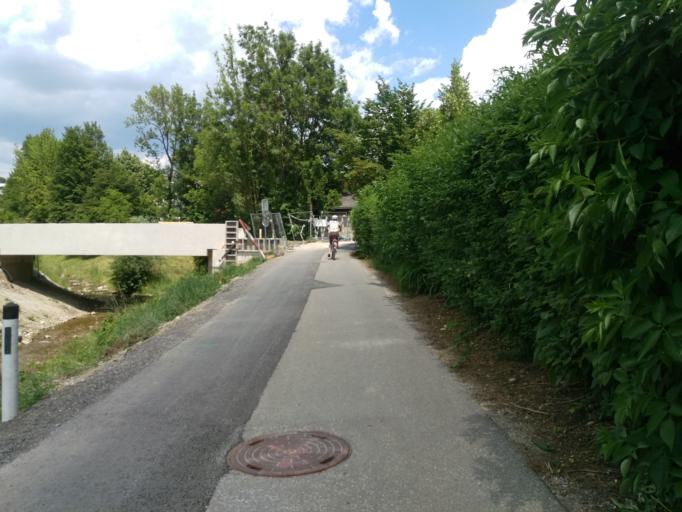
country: AT
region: Styria
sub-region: Graz Stadt
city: Graz
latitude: 47.0769
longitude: 15.4682
